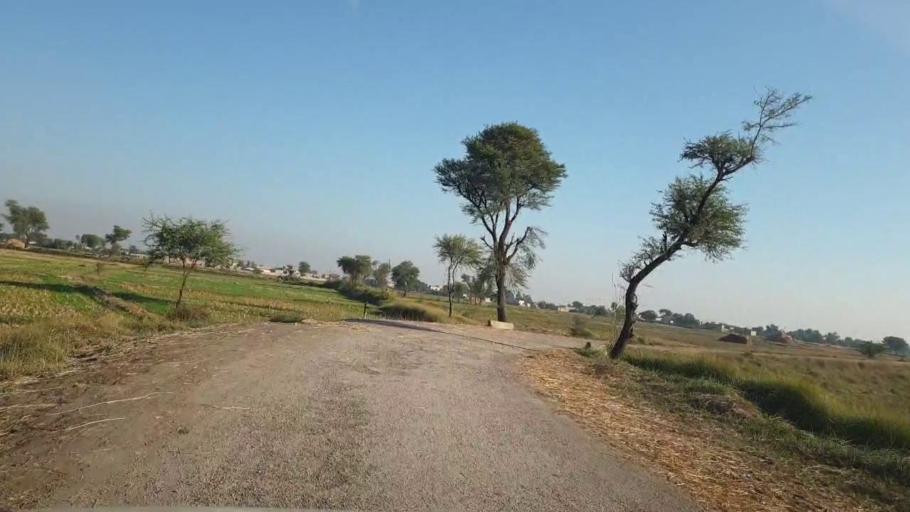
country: PK
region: Sindh
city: Phulji
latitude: 26.9880
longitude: 67.6899
